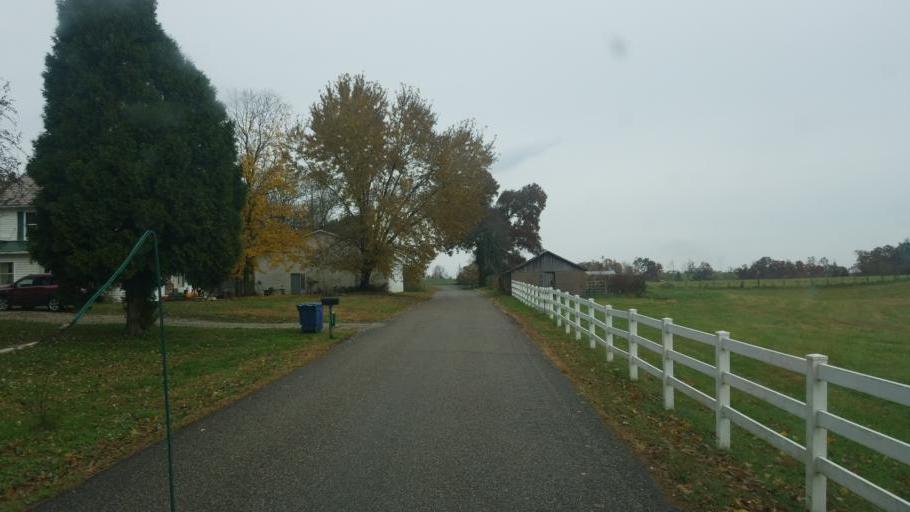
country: US
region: Ohio
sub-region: Washington County
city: Beverly
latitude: 39.5484
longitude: -81.7037
